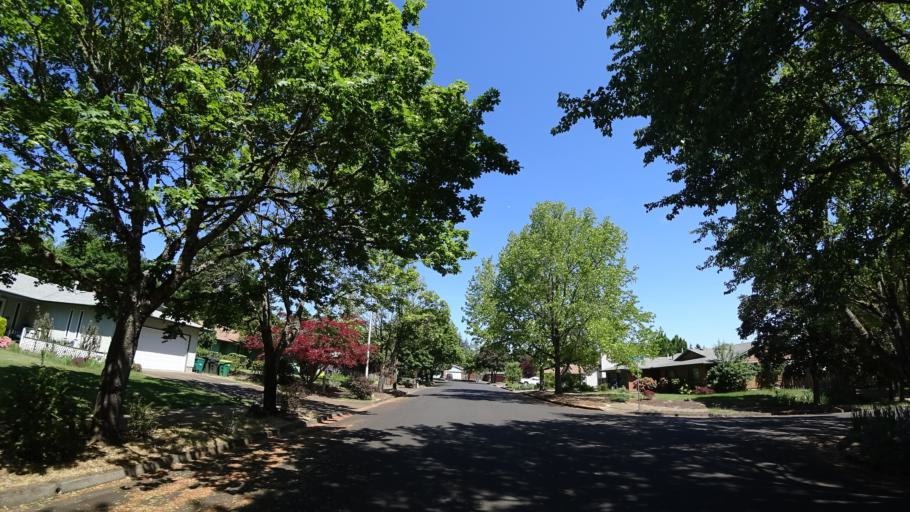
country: US
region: Oregon
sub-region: Washington County
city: Tigard
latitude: 45.4465
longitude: -122.8075
